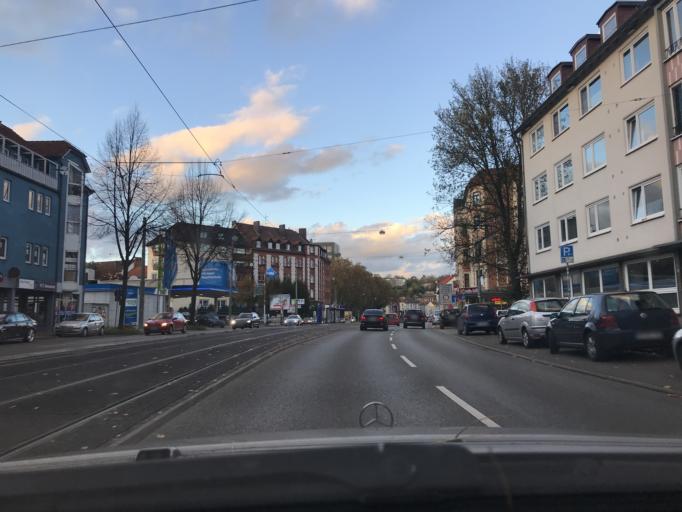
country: DE
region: Hesse
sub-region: Regierungsbezirk Kassel
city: Kassel
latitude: 51.3027
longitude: 9.4832
